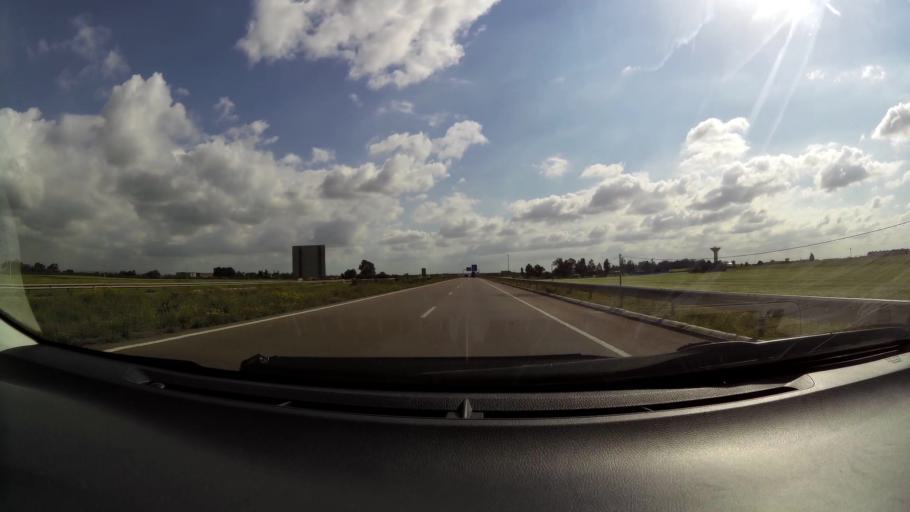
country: MA
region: Chaouia-Ouardigha
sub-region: Settat Province
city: Berrechid
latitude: 33.2557
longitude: -7.5591
